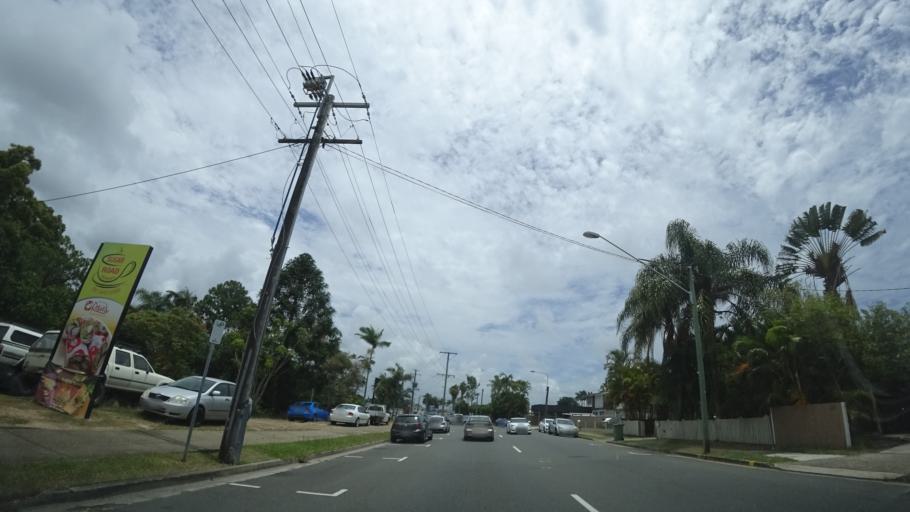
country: AU
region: Queensland
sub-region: Sunshine Coast
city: Mooloolaba
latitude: -26.6678
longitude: 153.0938
